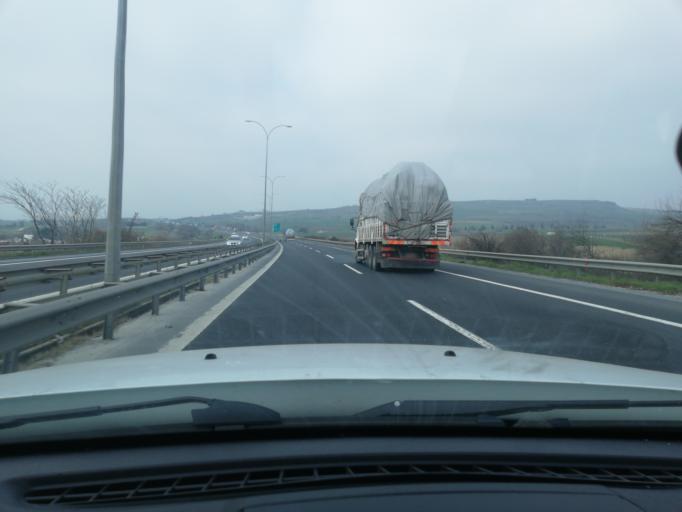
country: TR
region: Istanbul
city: Celaliye
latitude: 41.0638
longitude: 28.4054
